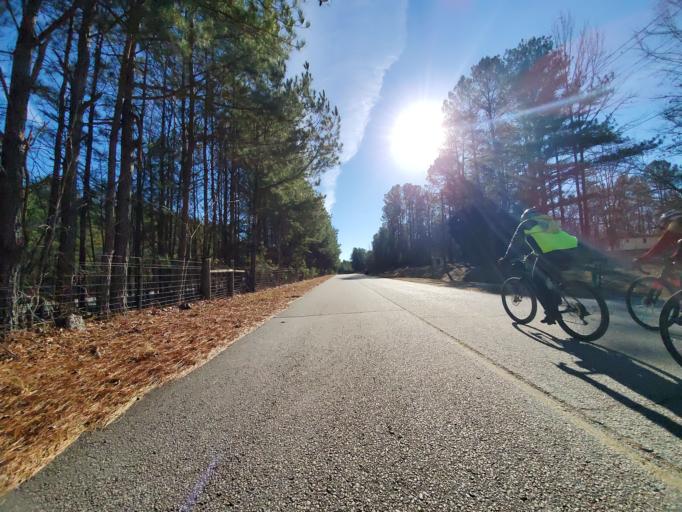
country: US
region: Georgia
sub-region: Fulton County
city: Chattahoochee Hills
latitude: 33.5728
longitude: -84.7935
